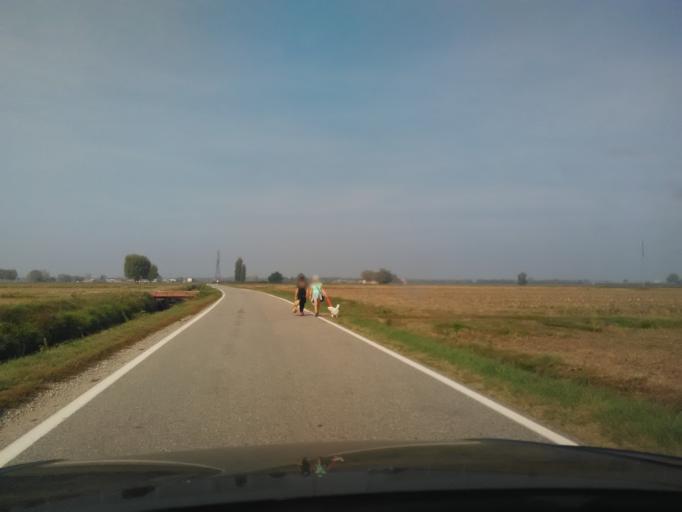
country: IT
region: Piedmont
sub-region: Provincia di Vercelli
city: Tronzano Vercellese
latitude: 45.3497
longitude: 8.1639
